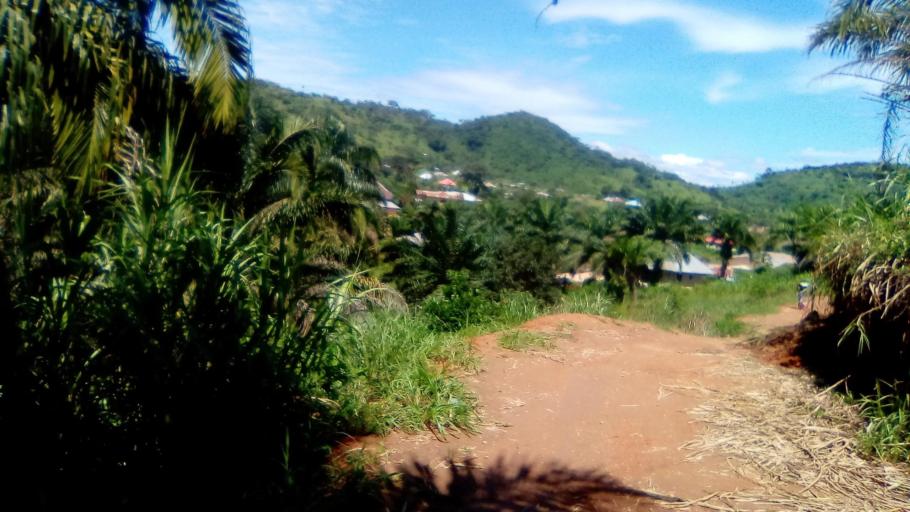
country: SL
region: Eastern Province
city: Simbakoro
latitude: 8.6320
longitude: -10.9958
